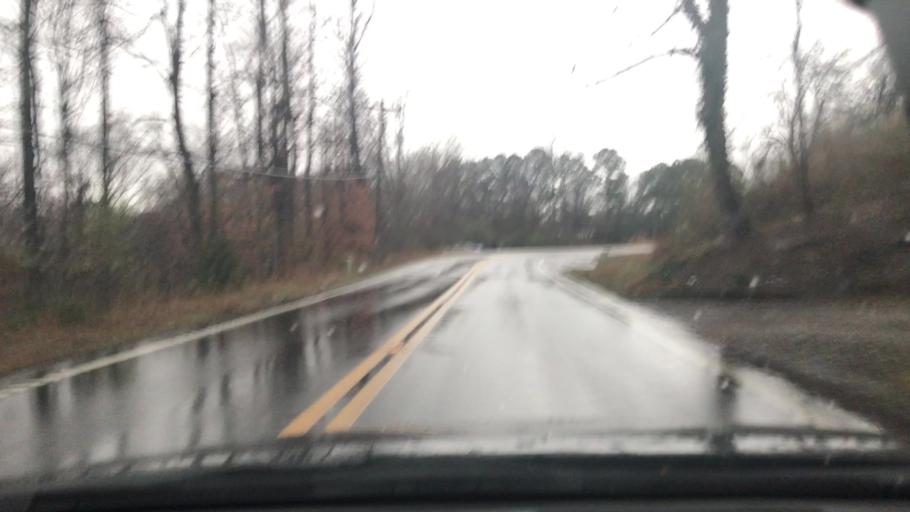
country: US
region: Tennessee
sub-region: Cheatham County
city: Ashland City
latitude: 36.2888
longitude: -87.1501
